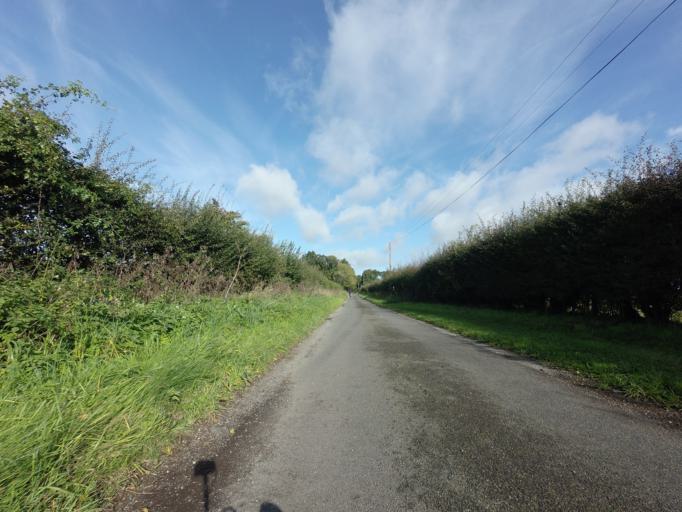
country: GB
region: England
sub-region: Norfolk
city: Fakenham
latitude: 52.8841
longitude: 0.6842
